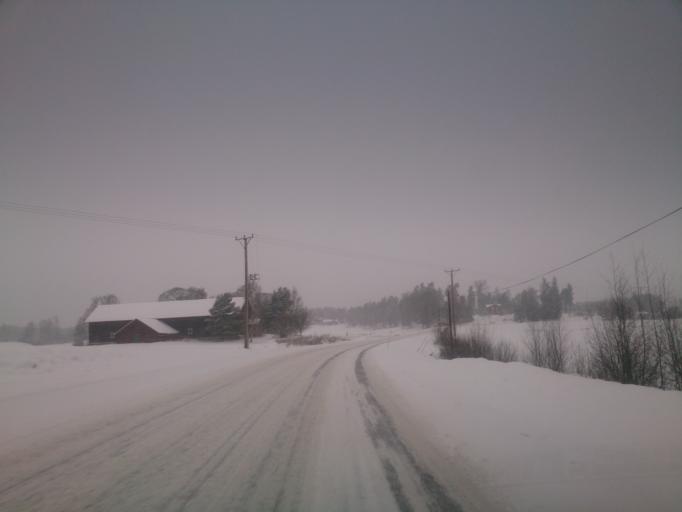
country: SE
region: OEstergoetland
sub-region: Finspangs Kommun
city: Finspang
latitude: 58.6713
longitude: 15.7562
